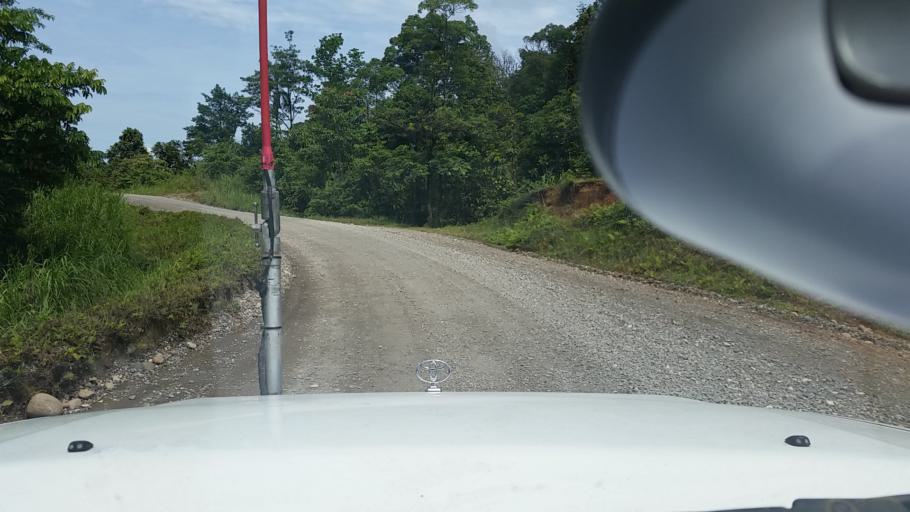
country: PG
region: Western Province
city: Kiunga
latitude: -5.8391
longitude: 141.1707
